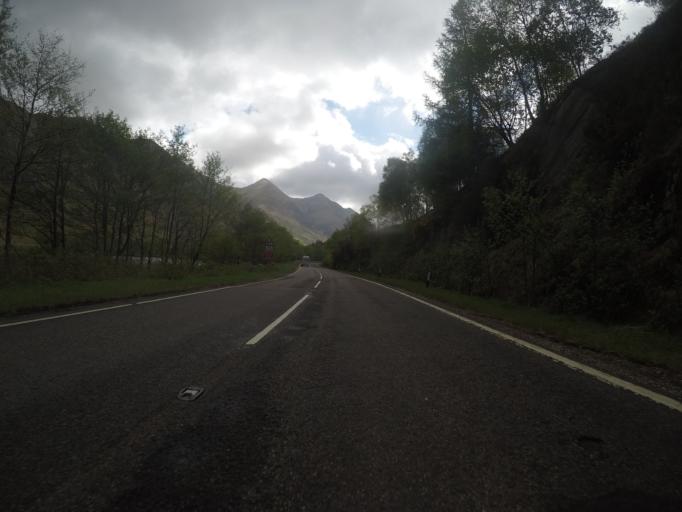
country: GB
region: Scotland
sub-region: Highland
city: Fort William
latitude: 57.2091
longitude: -5.4078
